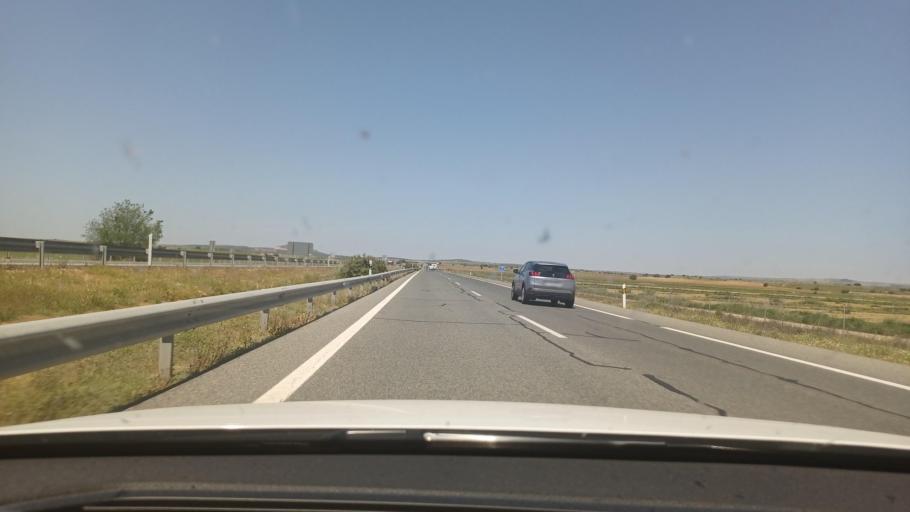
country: ES
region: Castille-La Mancha
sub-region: Provincia de Albacete
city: Bonete
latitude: 38.8768
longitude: -1.3681
